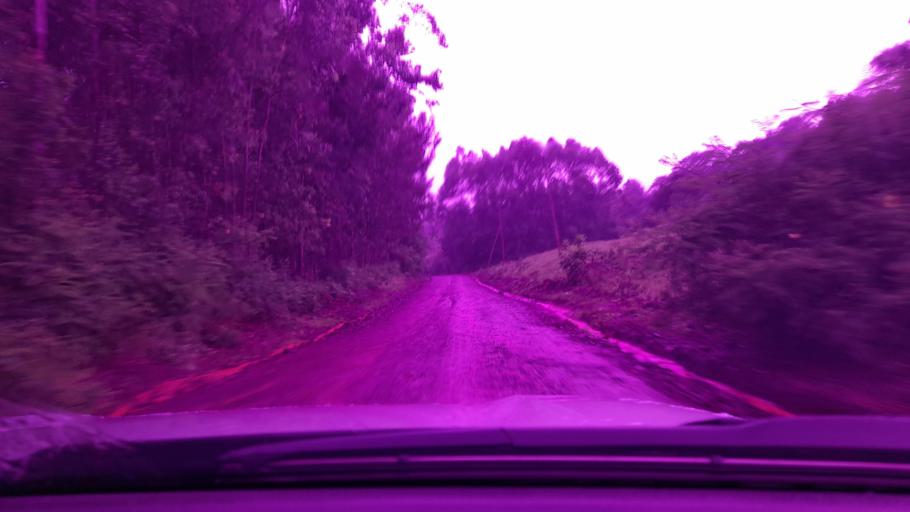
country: ET
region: Oromiya
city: Metu
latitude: 8.3321
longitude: 35.6051
